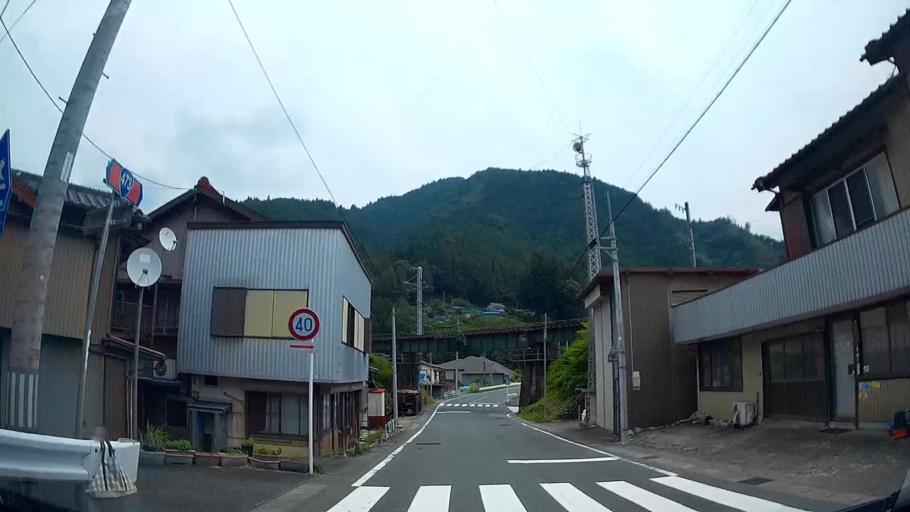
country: JP
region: Shizuoka
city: Mori
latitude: 35.0928
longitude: 137.8116
